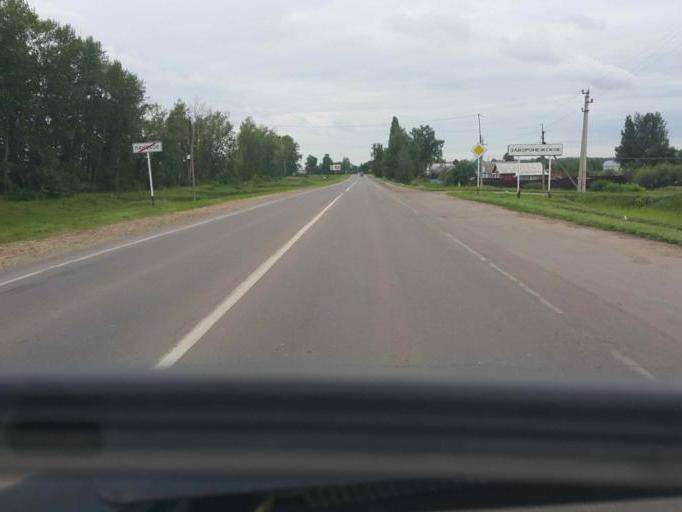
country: RU
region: Tambov
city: Zavoronezhskoye
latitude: 52.8894
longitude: 40.5673
